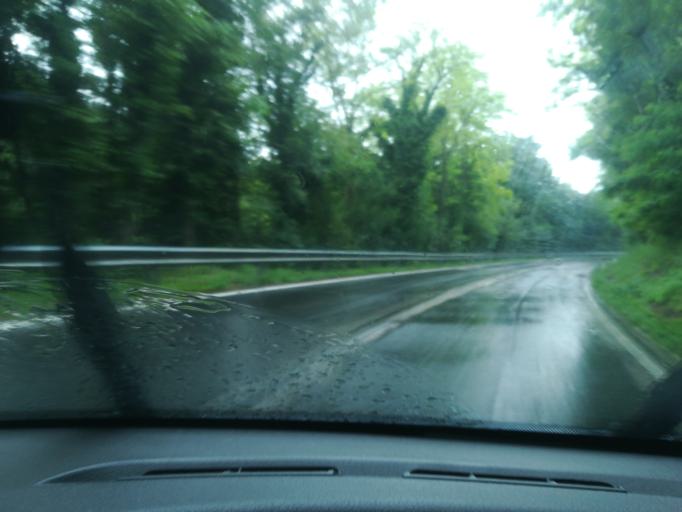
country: IT
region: The Marches
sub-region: Provincia di Macerata
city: Sarnano
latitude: 43.0432
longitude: 13.2858
